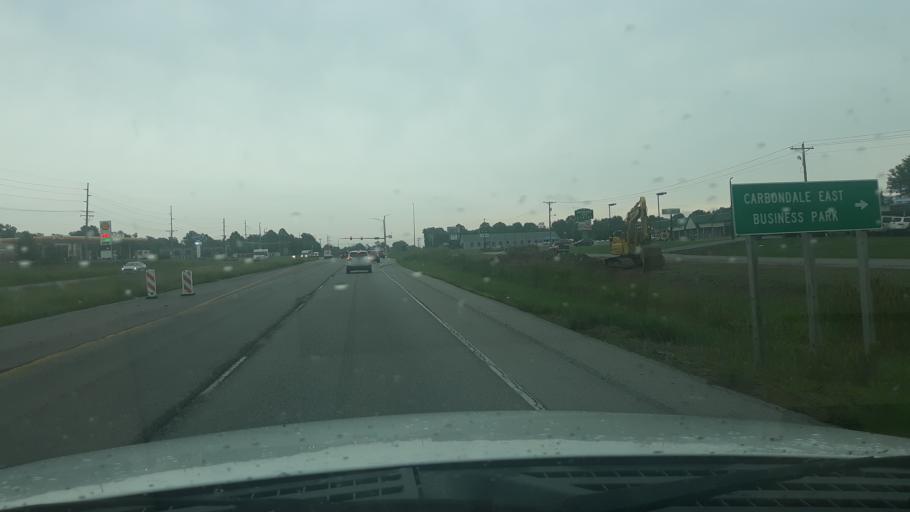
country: US
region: Illinois
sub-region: Jackson County
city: Carbondale
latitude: 37.7418
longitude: -89.1640
